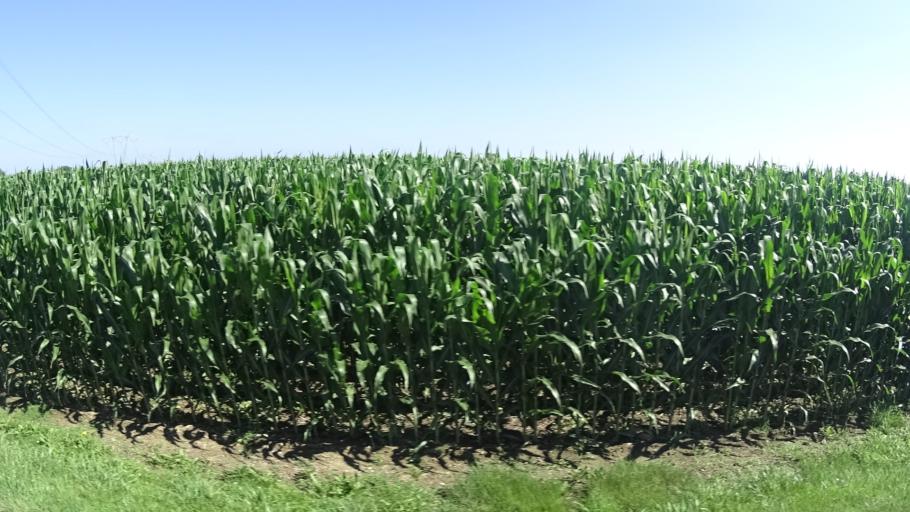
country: US
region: Indiana
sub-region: Madison County
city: Ingalls
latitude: 39.9879
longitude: -85.8117
